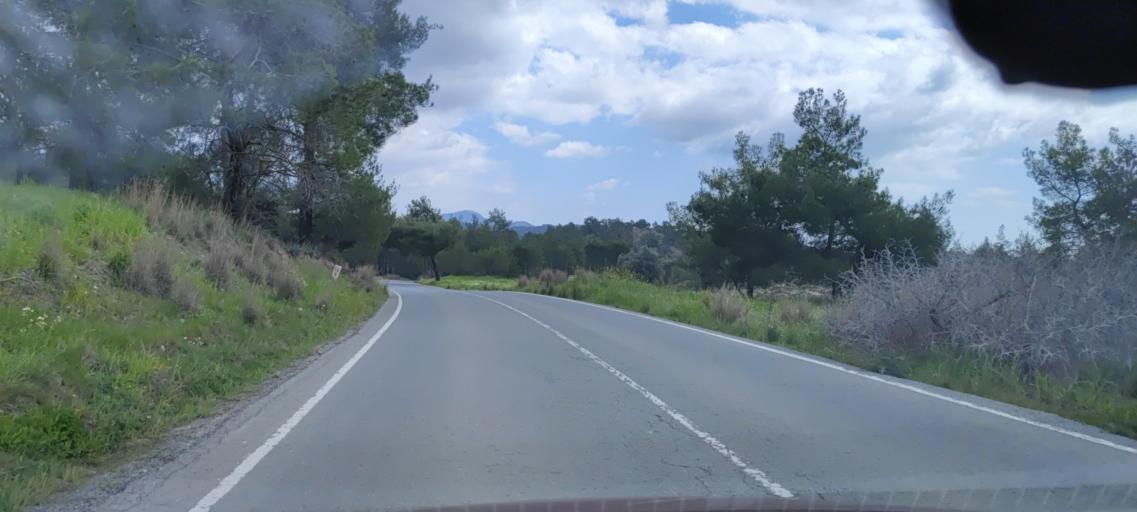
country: CY
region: Larnaka
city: Kornos
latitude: 34.9186
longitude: 33.3548
